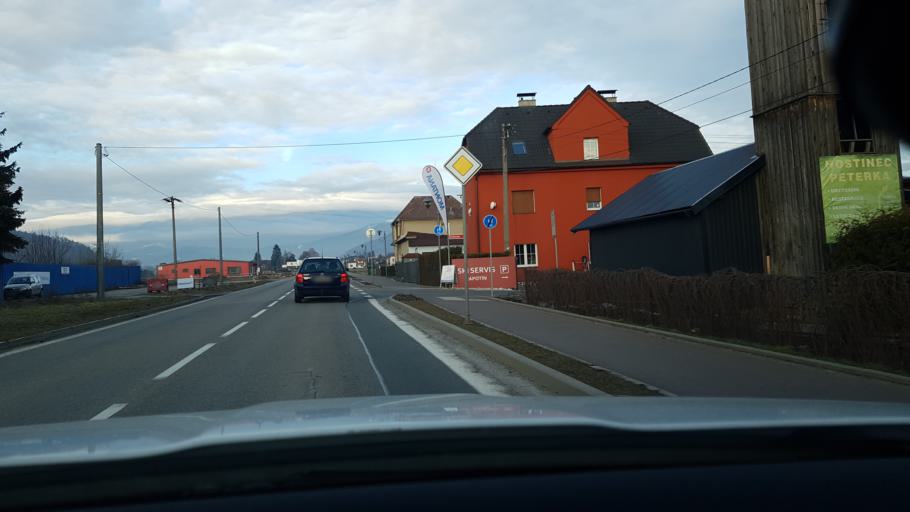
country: CZ
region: Olomoucky
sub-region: Okres Sumperk
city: Vikyrovice
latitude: 49.9958
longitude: 17.0116
